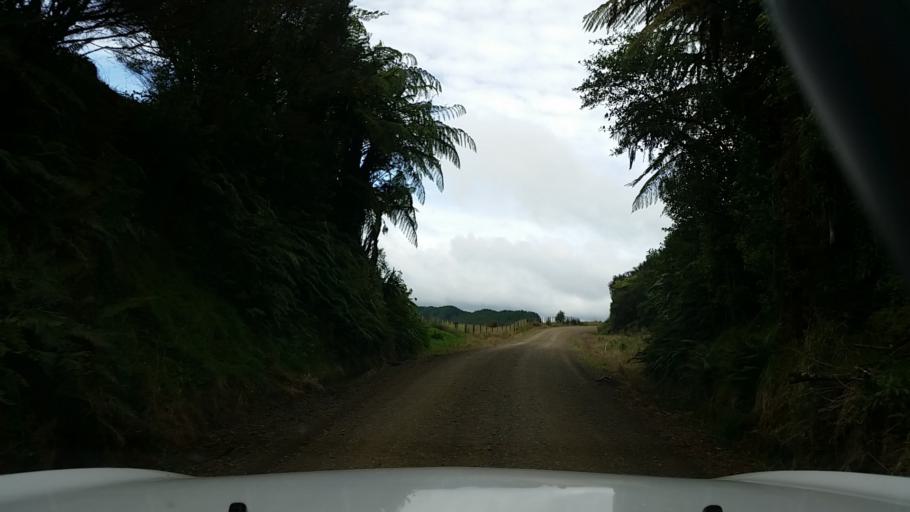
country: NZ
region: Taranaki
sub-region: New Plymouth District
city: Waitara
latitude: -38.9147
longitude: 174.7688
